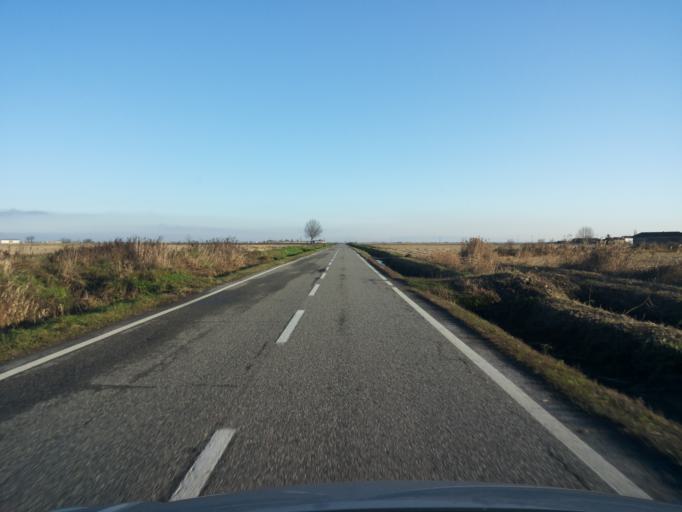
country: IT
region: Piedmont
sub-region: Provincia di Vercelli
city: Salasco
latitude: 45.3060
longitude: 8.2544
